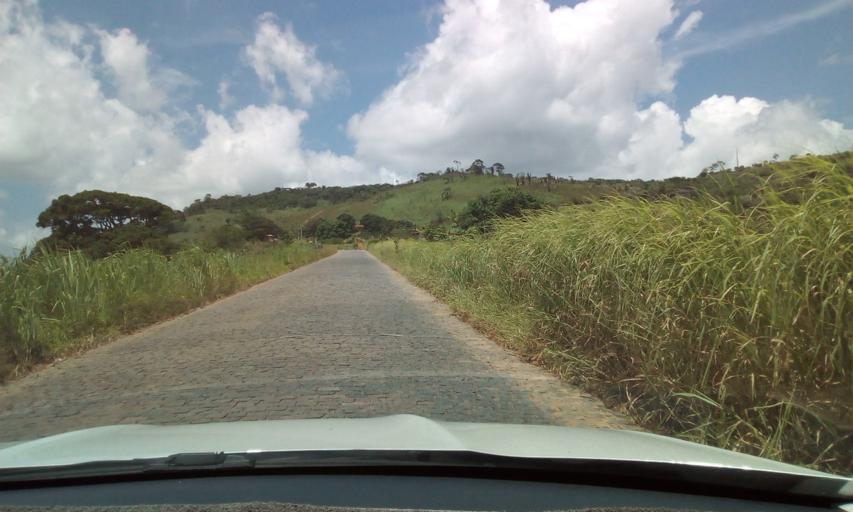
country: BR
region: Pernambuco
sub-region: Bonito
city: Bonito
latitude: -8.4914
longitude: -35.7273
